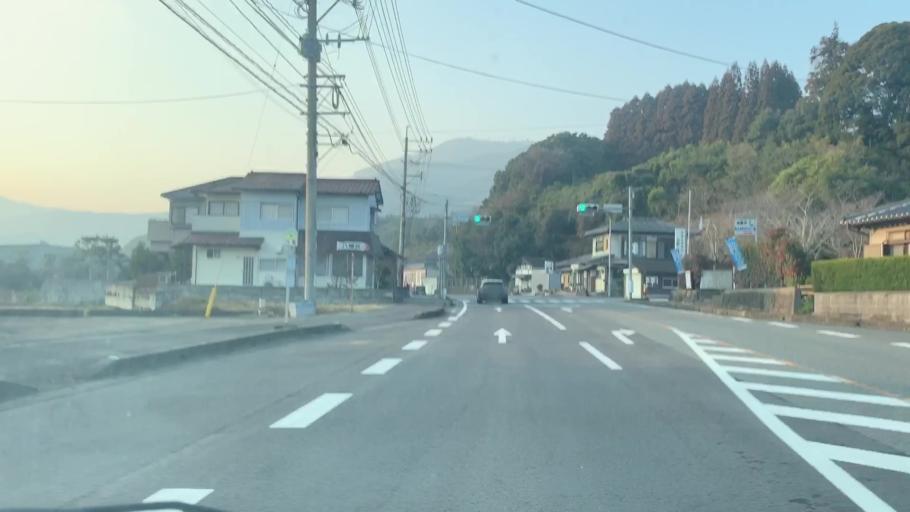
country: JP
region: Saga Prefecture
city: Takeocho-takeo
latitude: 33.2626
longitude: 130.0575
